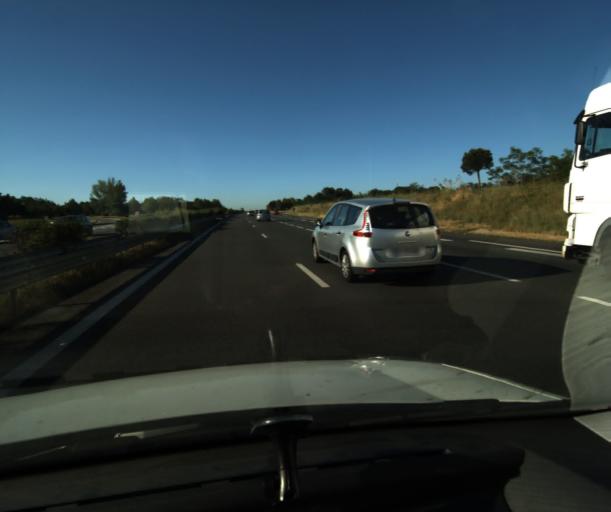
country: FR
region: Midi-Pyrenees
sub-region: Departement du Tarn-et-Garonne
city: Campsas
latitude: 43.8901
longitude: 1.3173
